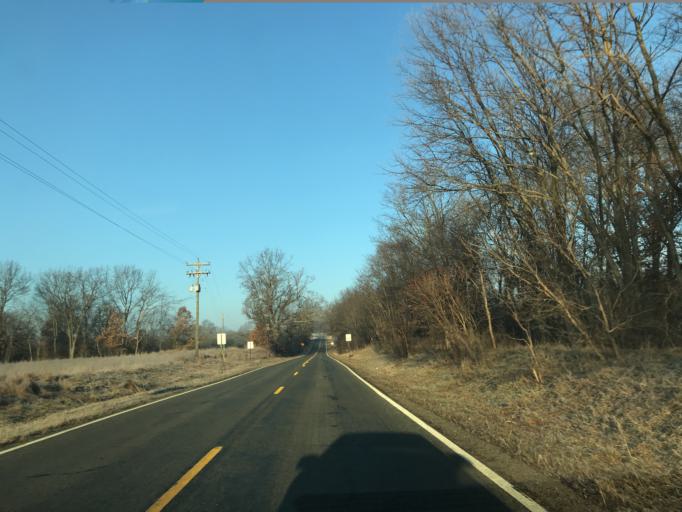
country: US
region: Michigan
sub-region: Eaton County
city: Eaton Rapids
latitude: 42.4480
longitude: -84.5684
